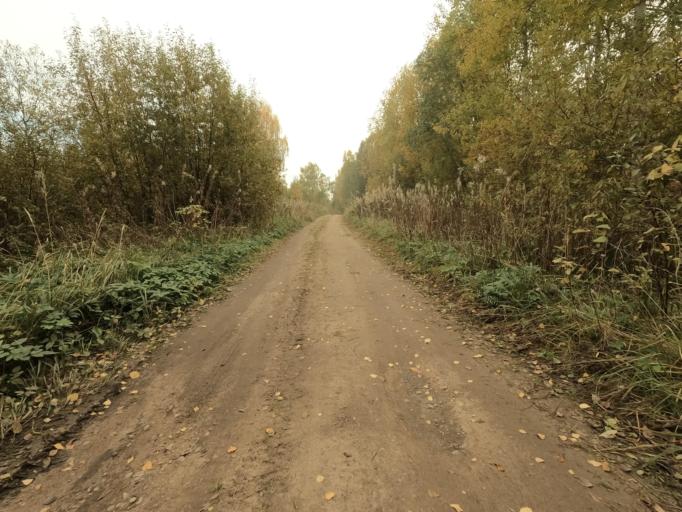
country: RU
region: Novgorod
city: Pankovka
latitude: 58.8712
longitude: 30.8952
